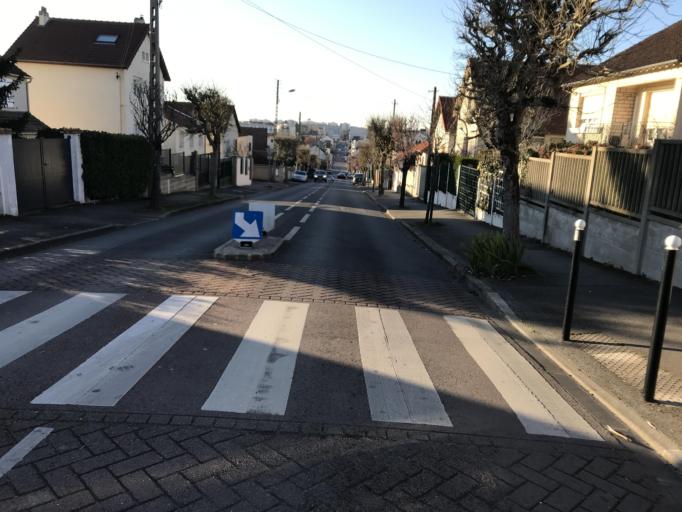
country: FR
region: Ile-de-France
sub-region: Departement de l'Essonne
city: Morangis
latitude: 48.6987
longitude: 2.3289
